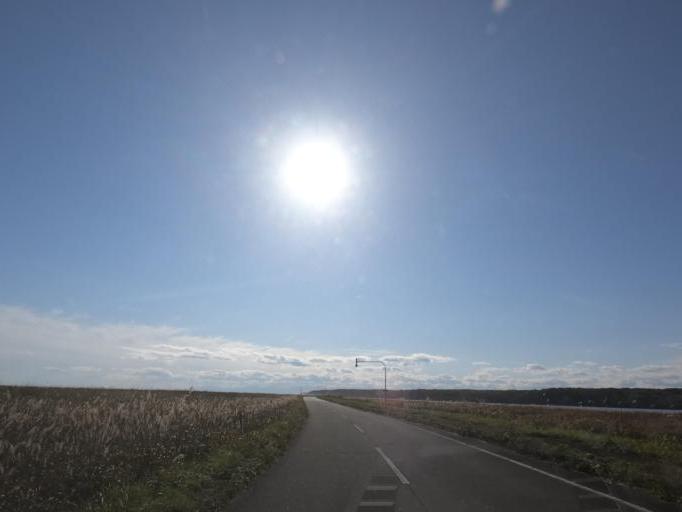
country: JP
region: Hokkaido
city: Obihiro
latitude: 42.5896
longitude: 143.5391
